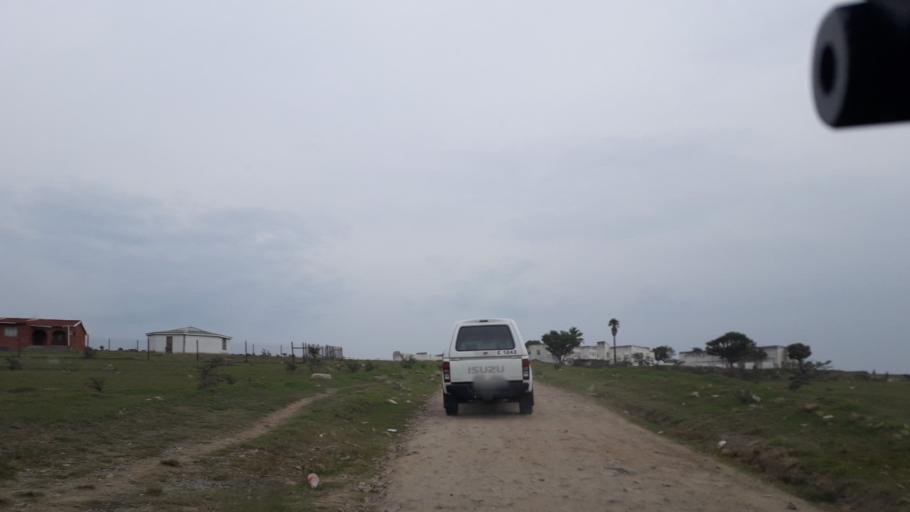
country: ZA
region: Eastern Cape
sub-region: Buffalo City Metropolitan Municipality
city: Bhisho
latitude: -32.8309
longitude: 27.3767
